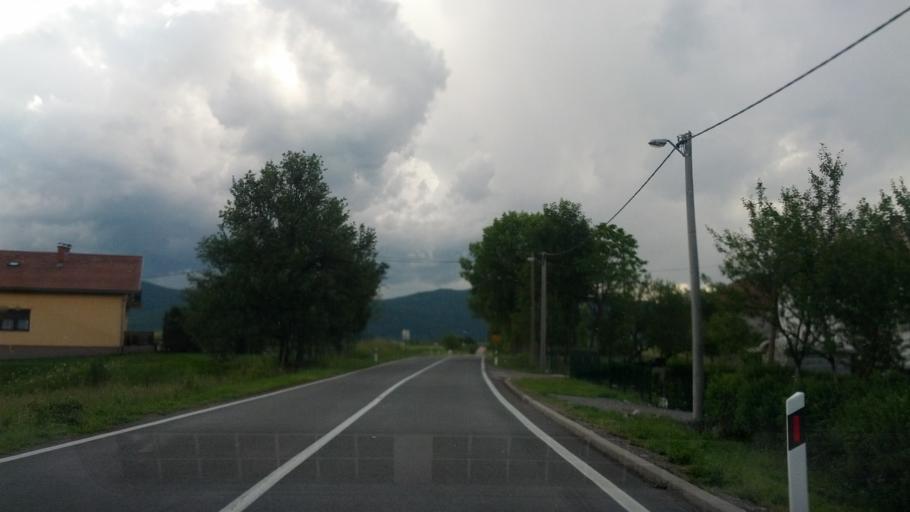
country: BA
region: Federation of Bosnia and Herzegovina
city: Izacic
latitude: 44.8781
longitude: 15.7726
